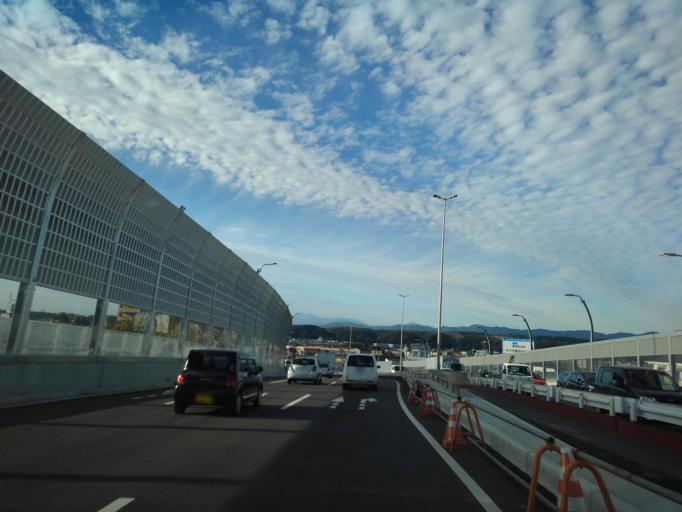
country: JP
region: Tokyo
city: Fussa
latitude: 35.7229
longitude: 139.3418
